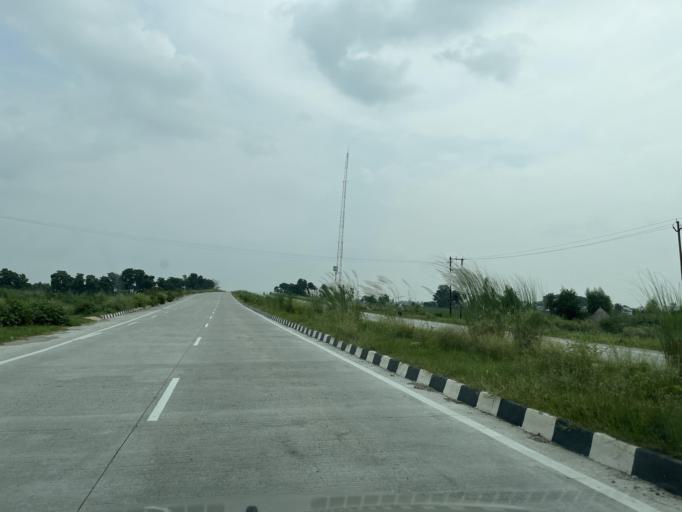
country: IN
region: Uttarakhand
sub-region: Udham Singh Nagar
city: Kashipur
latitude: 29.1929
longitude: 78.9375
